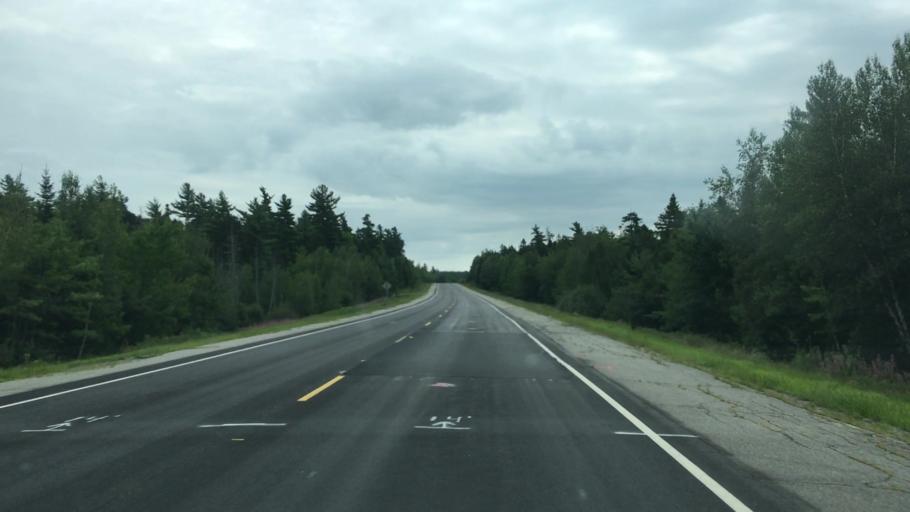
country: US
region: Maine
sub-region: Washington County
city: Addison
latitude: 44.9058
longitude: -67.8221
